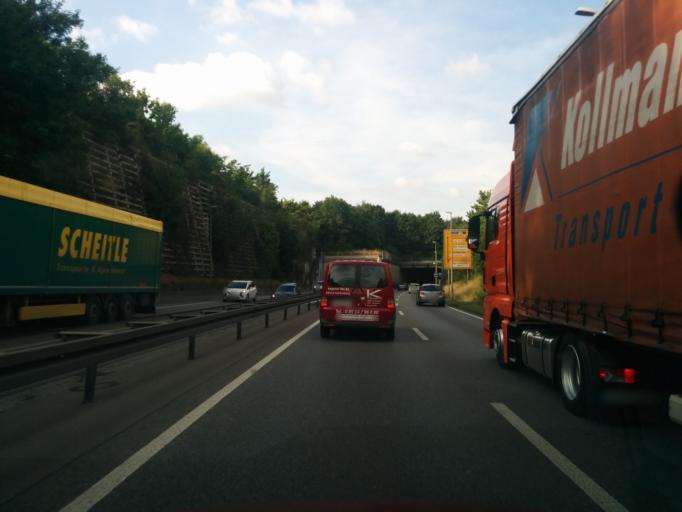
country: DE
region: Bavaria
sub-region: Swabia
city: Gersthofen
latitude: 48.3944
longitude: 10.8633
